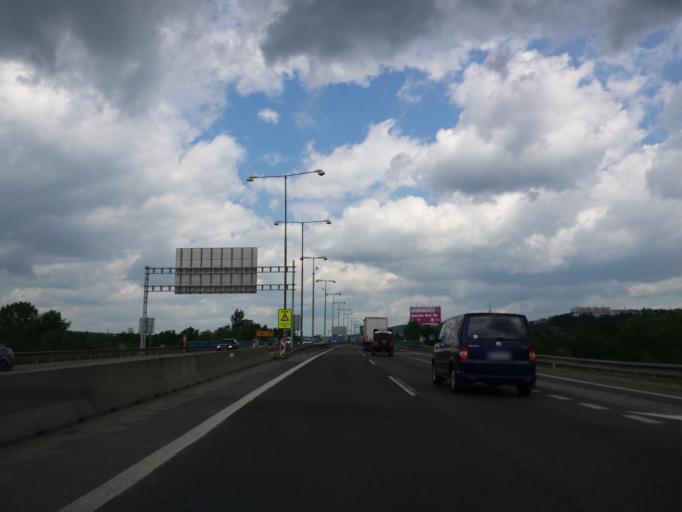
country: SK
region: Bratislavsky
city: Bratislava
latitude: 48.1367
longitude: 17.0745
